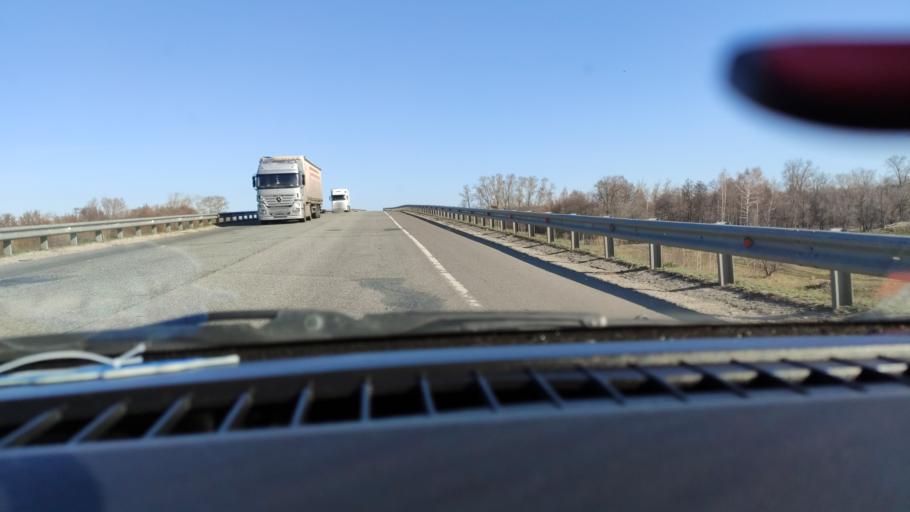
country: RU
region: Samara
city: Varlamovo
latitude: 53.1638
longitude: 48.2824
